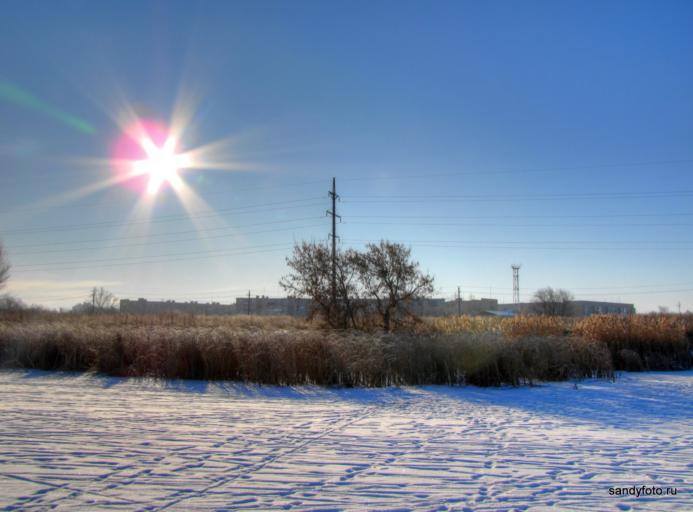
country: RU
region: Chelyabinsk
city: Troitsk
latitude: 54.0955
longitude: 61.5537
